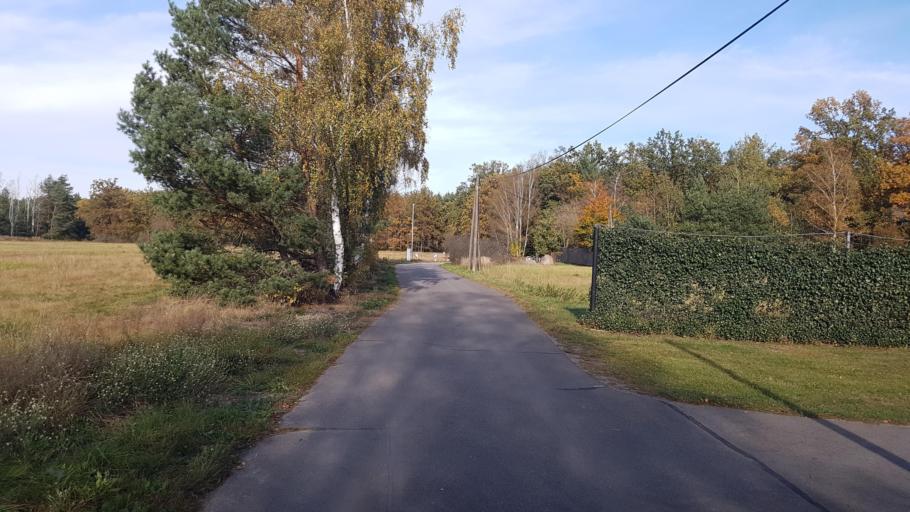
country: DE
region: Brandenburg
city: Tettau
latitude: 51.4305
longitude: 13.7573
